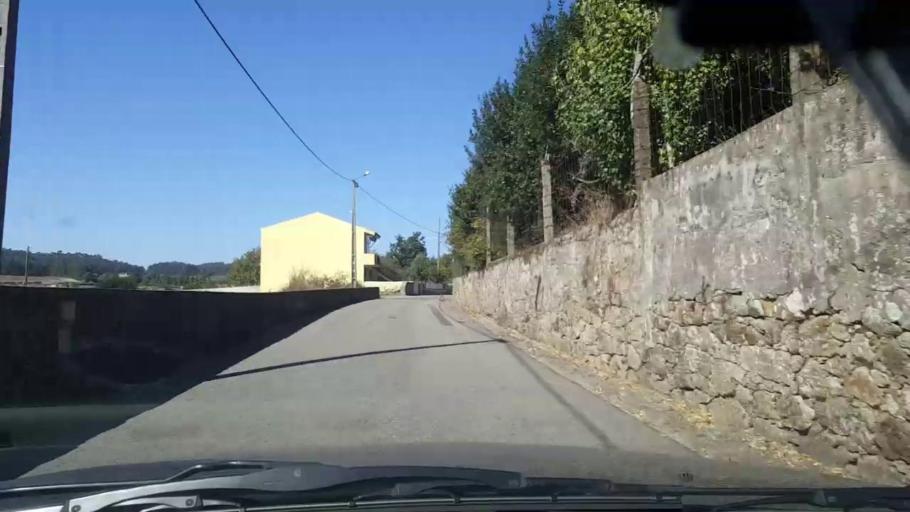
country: PT
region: Braga
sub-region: Vila Nova de Famalicao
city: Ribeirao
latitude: 41.3712
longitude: -8.6448
